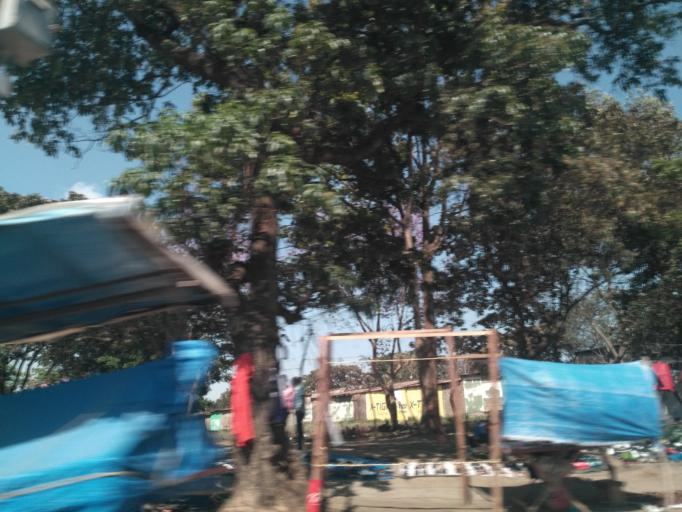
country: TZ
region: Arusha
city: Arusha
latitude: -3.3688
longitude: 36.6851
